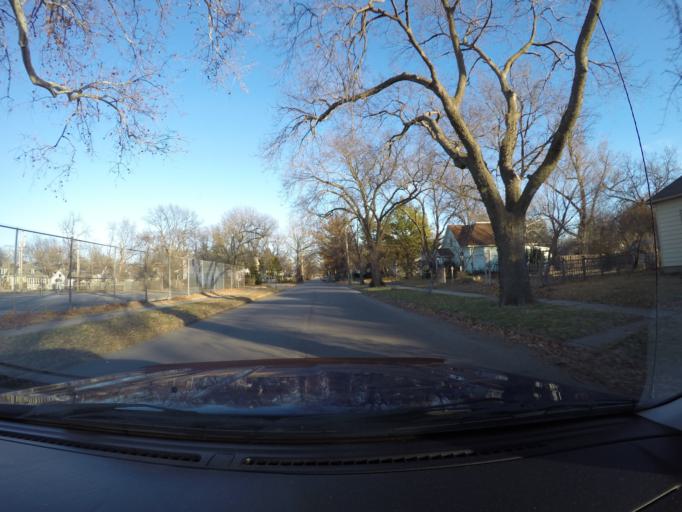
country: US
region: Kansas
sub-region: Riley County
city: Manhattan
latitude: 39.1774
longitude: -96.5707
